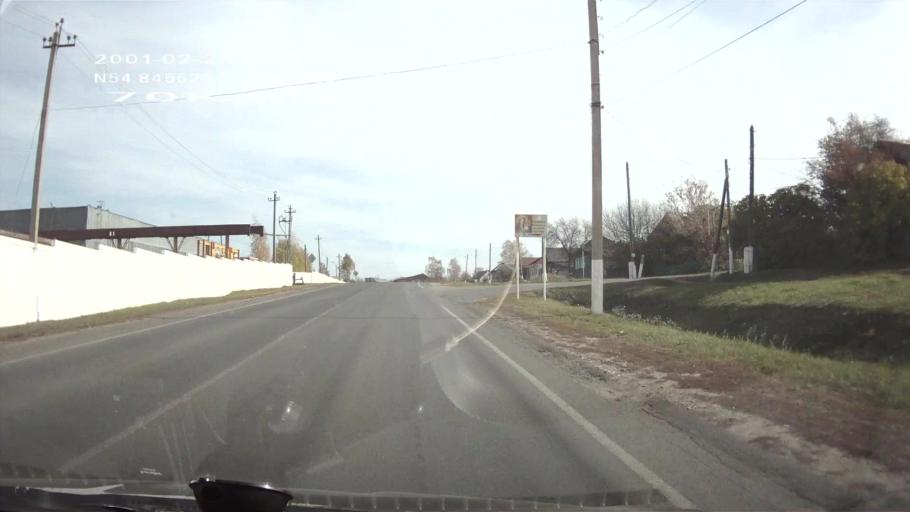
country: RU
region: Mordoviya
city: Turgenevo
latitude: 54.8455
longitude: 46.3432
